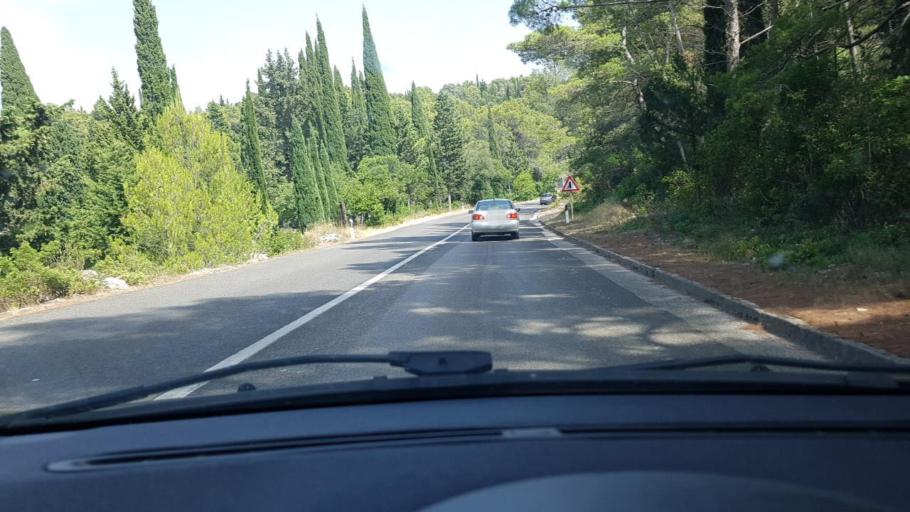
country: HR
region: Dubrovacko-Neretvanska
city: Korcula
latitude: 42.9545
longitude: 17.1297
